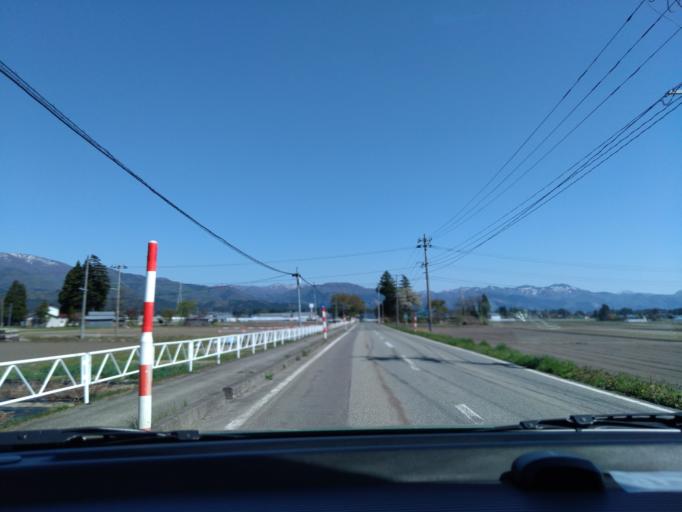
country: JP
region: Akita
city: Kakunodatemachi
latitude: 39.5739
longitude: 140.5748
